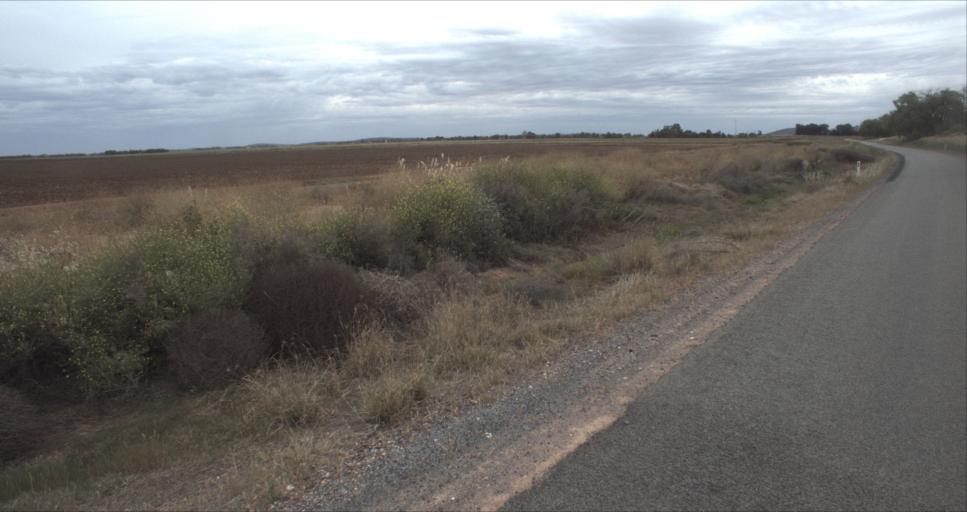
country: AU
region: New South Wales
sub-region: Leeton
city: Leeton
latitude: -34.4300
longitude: 146.3776
